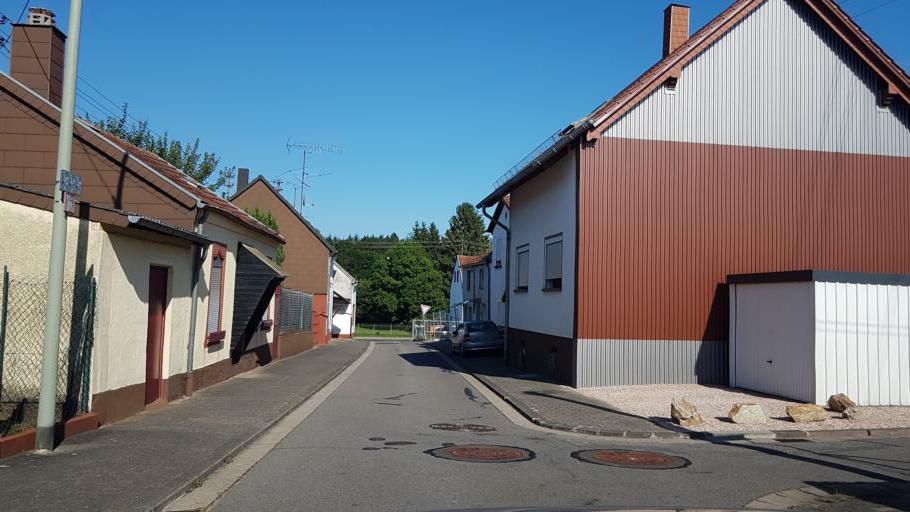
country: DE
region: Saarland
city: Weiskirchen
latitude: 49.5390
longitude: 6.8332
